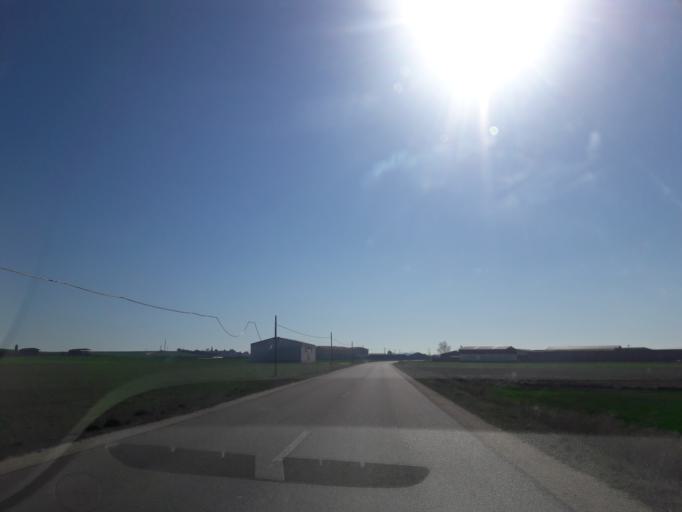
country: ES
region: Castille and Leon
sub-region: Provincia de Salamanca
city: Macotera
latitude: 40.8347
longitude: -5.2997
